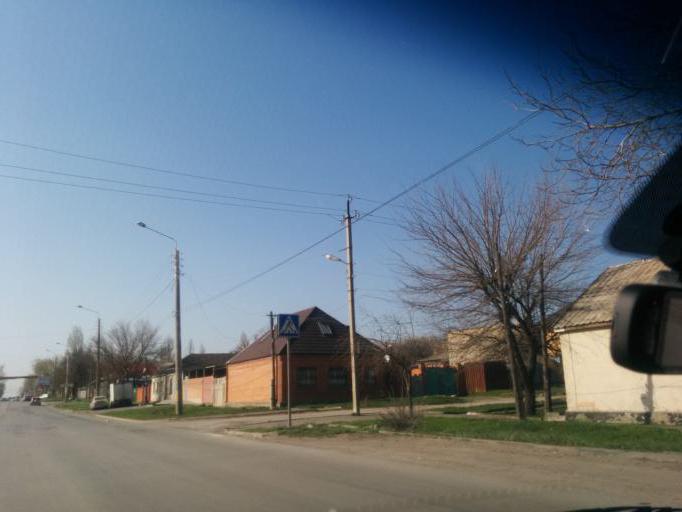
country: RU
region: Rostov
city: Shakhty
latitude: 47.7015
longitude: 40.2011
